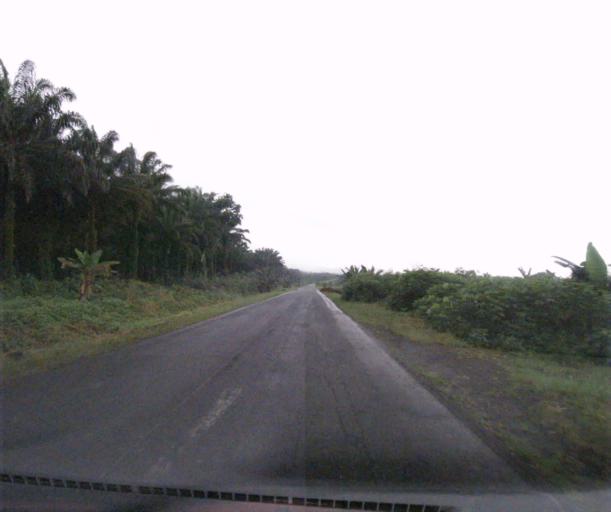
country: CM
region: South-West Province
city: Idenao
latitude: 4.1980
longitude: 9.0023
